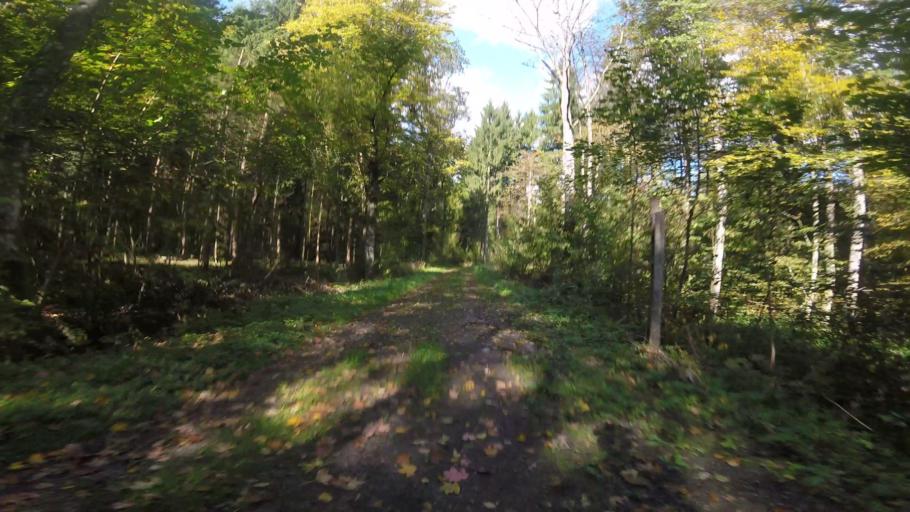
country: DE
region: Baden-Wuerttemberg
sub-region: Regierungsbezirk Stuttgart
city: Aspach
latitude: 48.9834
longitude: 9.3896
